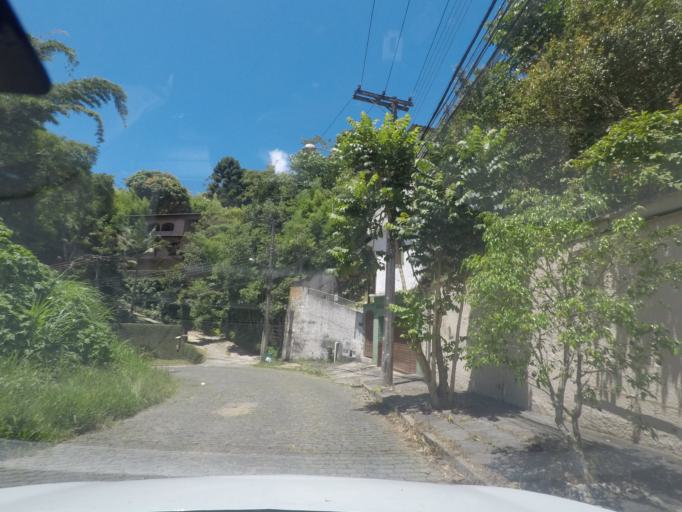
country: BR
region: Rio de Janeiro
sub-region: Teresopolis
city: Teresopolis
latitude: -22.4205
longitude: -42.9832
